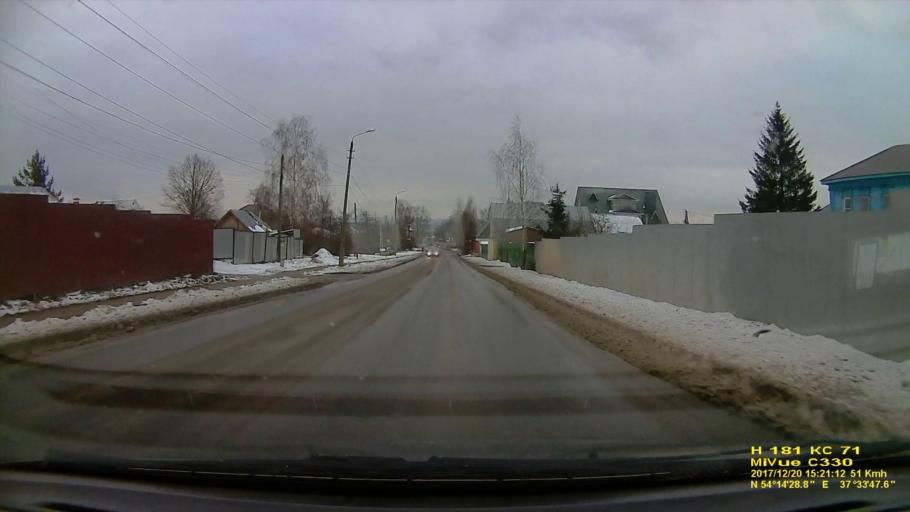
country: RU
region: Tula
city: Gorelki
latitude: 54.2411
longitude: 37.5633
